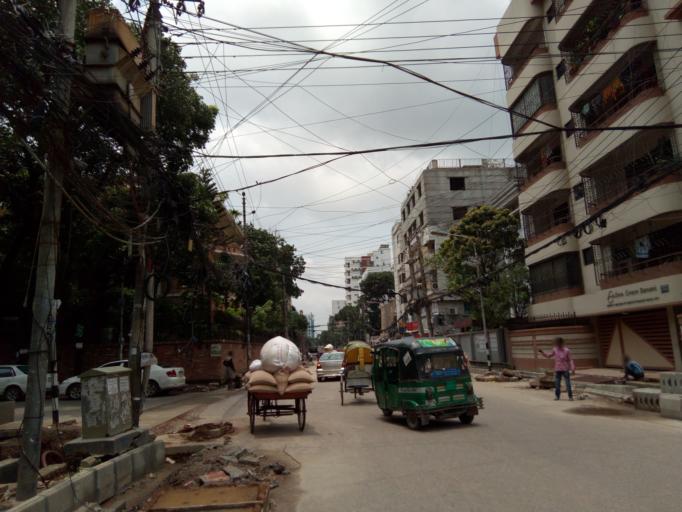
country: BD
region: Dhaka
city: Paltan
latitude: 23.7897
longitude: 90.4037
